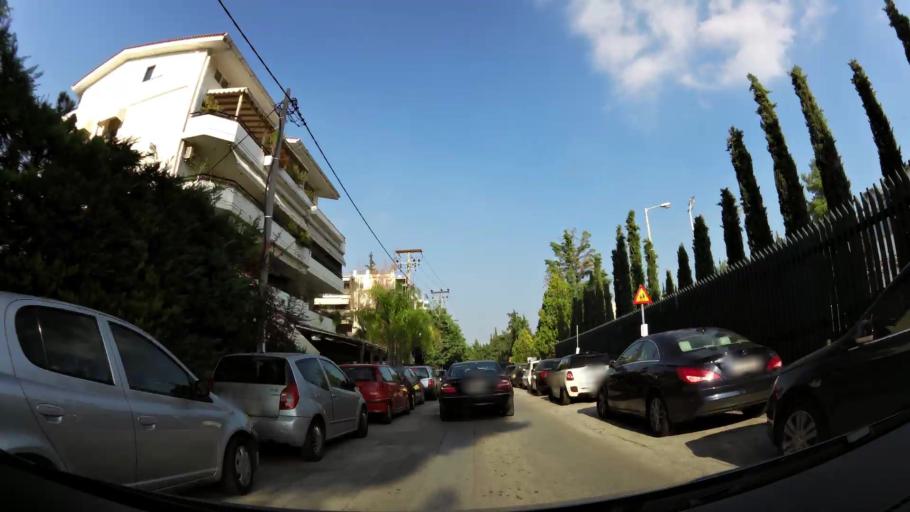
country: GR
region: Attica
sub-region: Nomarchia Athinas
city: Agia Paraskevi
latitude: 38.0034
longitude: 23.8299
